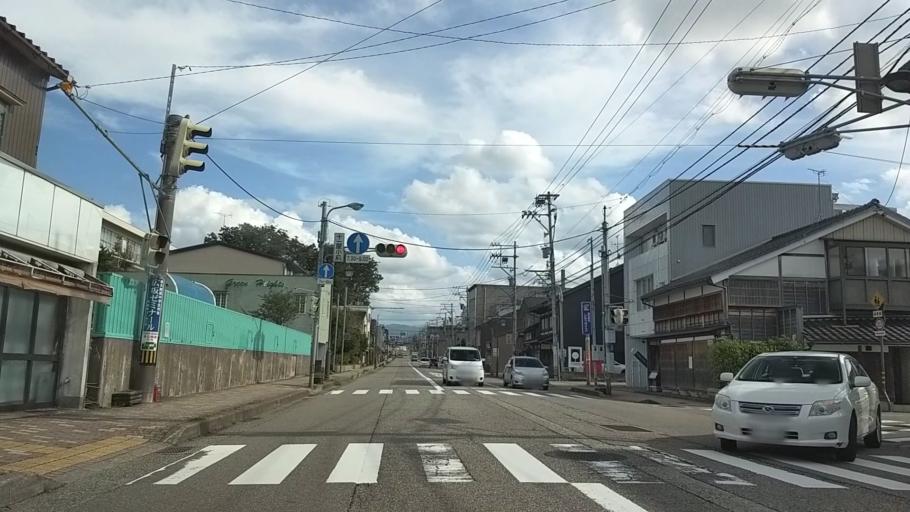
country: JP
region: Ishikawa
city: Nonoichi
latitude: 36.5457
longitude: 136.6599
